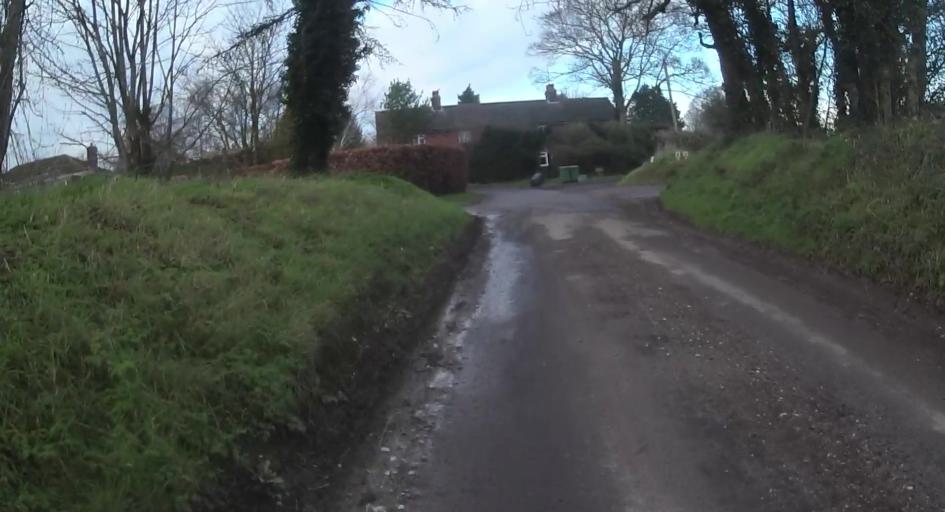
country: GB
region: England
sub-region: Hampshire
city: Basingstoke
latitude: 51.2816
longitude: -1.1569
